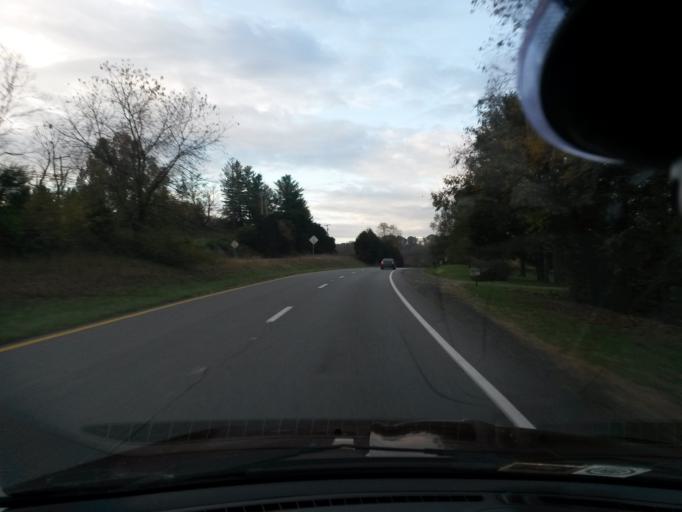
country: US
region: Virginia
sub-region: Botetourt County
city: Fincastle
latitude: 37.4903
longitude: -79.8777
